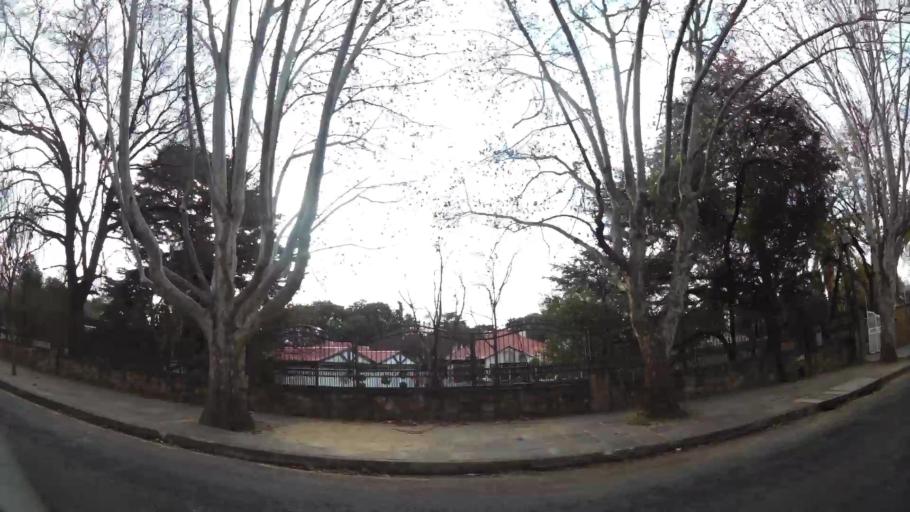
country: ZA
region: Gauteng
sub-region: Ekurhuleni Metropolitan Municipality
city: Germiston
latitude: -26.2350
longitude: 28.1705
